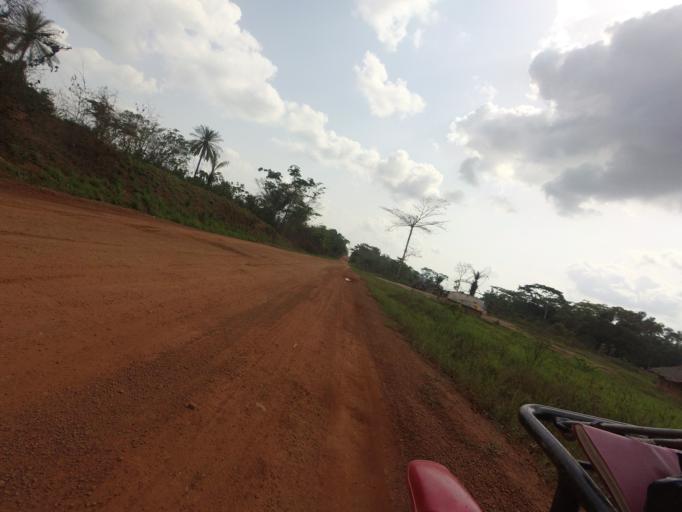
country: LR
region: Nimba
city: Sanniquellie
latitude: 7.3973
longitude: -8.6665
